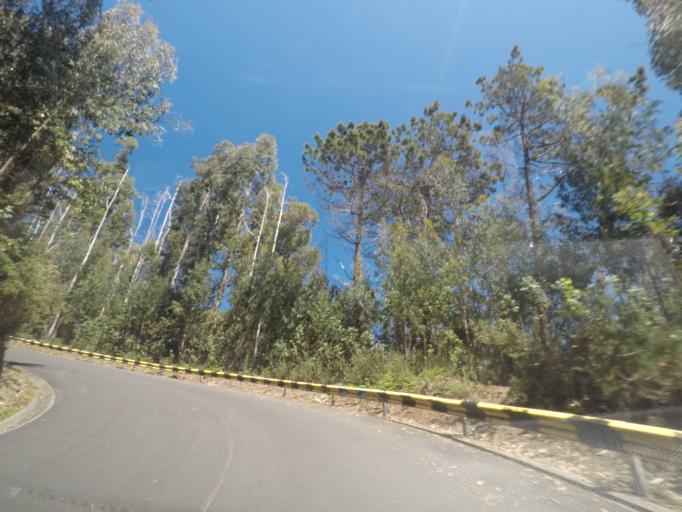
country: PT
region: Madeira
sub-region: Calheta
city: Arco da Calheta
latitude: 32.7383
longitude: -17.1289
